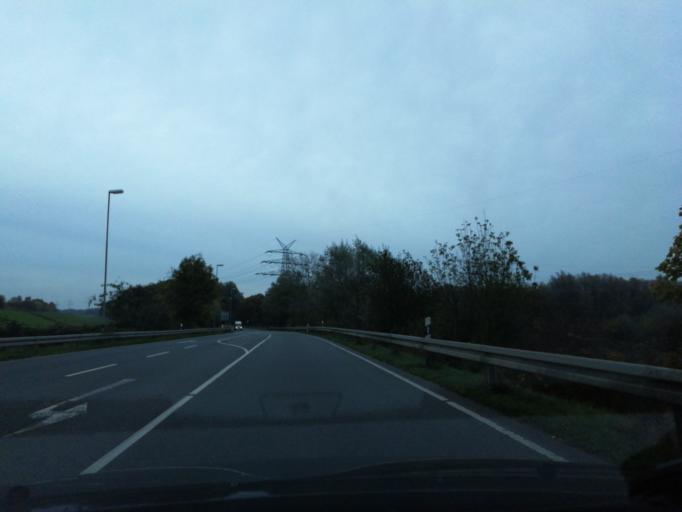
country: DE
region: Lower Saxony
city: Wilhelmshaven
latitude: 53.5605
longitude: 8.1193
